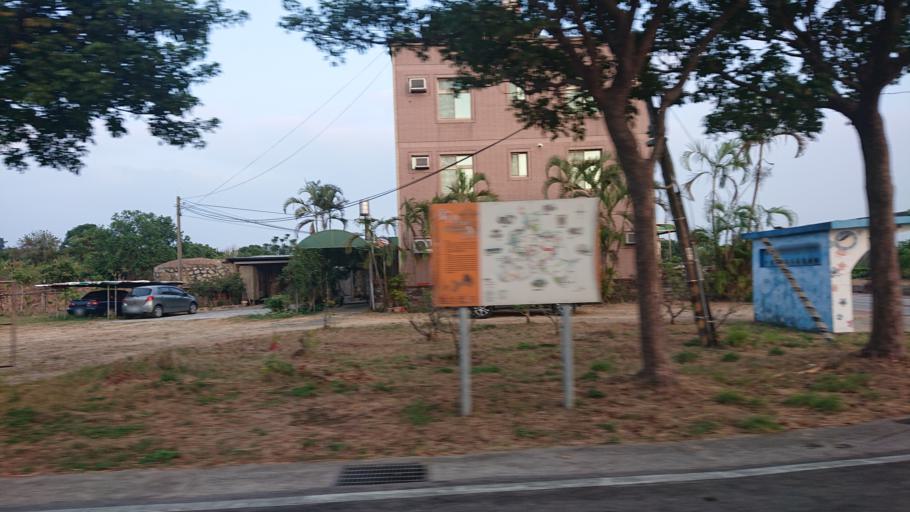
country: CN
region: Fujian
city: Dadeng
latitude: 24.4862
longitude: 118.4394
